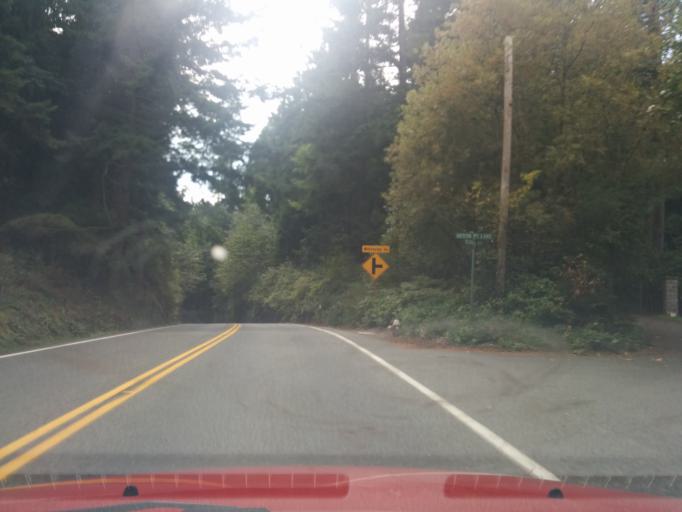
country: US
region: Washington
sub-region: Whatcom County
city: Bellingham
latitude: 48.6639
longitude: -122.4909
